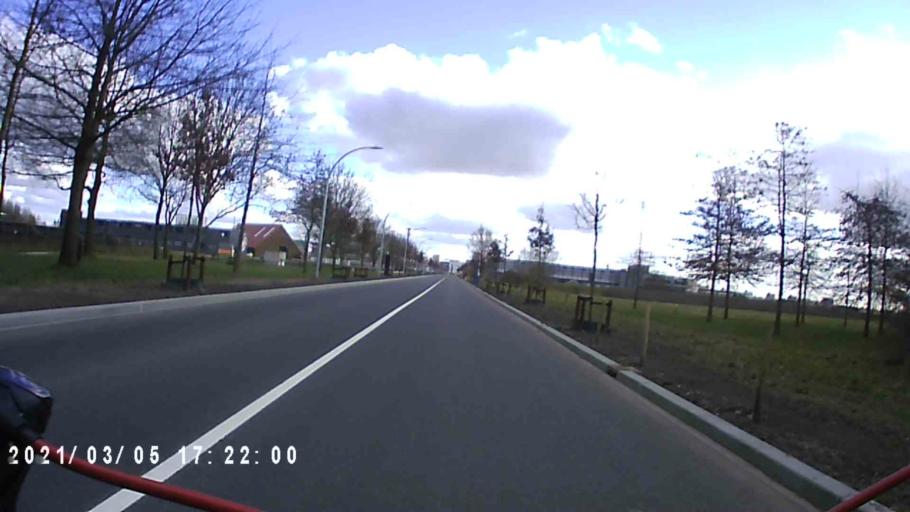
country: NL
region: Groningen
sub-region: Gemeente Groningen
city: Korrewegwijk
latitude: 53.2489
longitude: 6.5271
